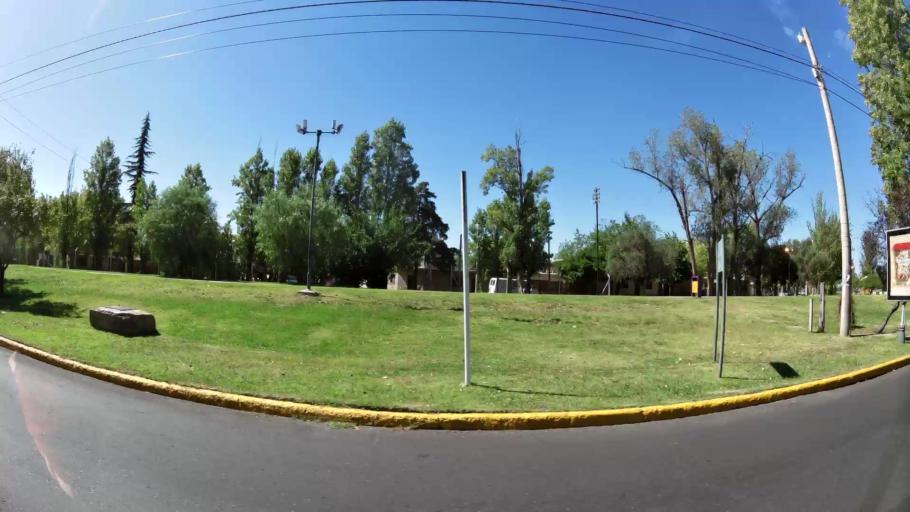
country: AR
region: Mendoza
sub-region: Departamento de Godoy Cruz
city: Godoy Cruz
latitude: -32.9499
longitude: -68.8543
